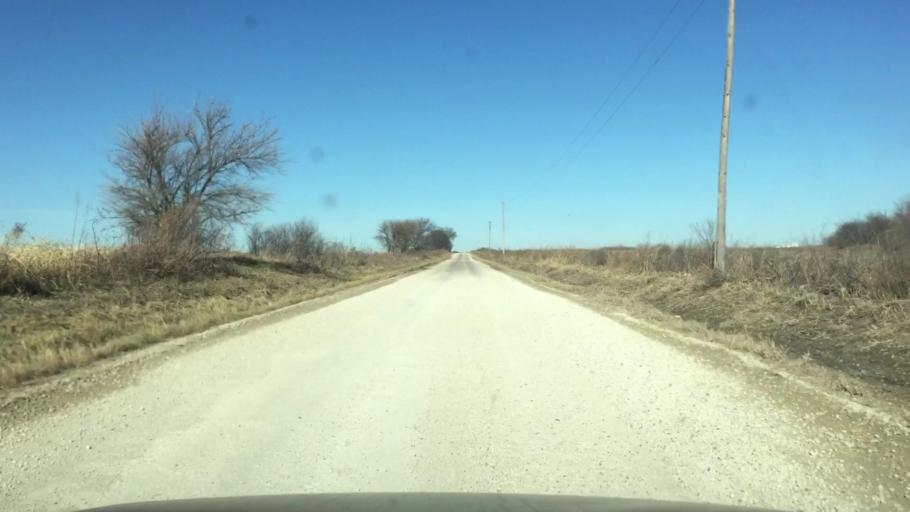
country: US
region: Kansas
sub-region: Allen County
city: Humboldt
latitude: 37.8531
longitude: -95.3910
